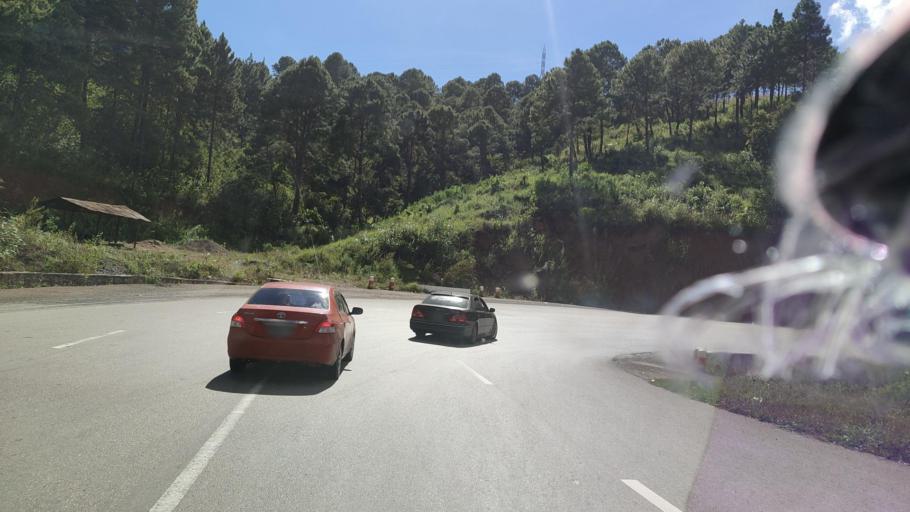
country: MM
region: Mandalay
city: Yamethin
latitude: 20.6533
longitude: 96.5481
